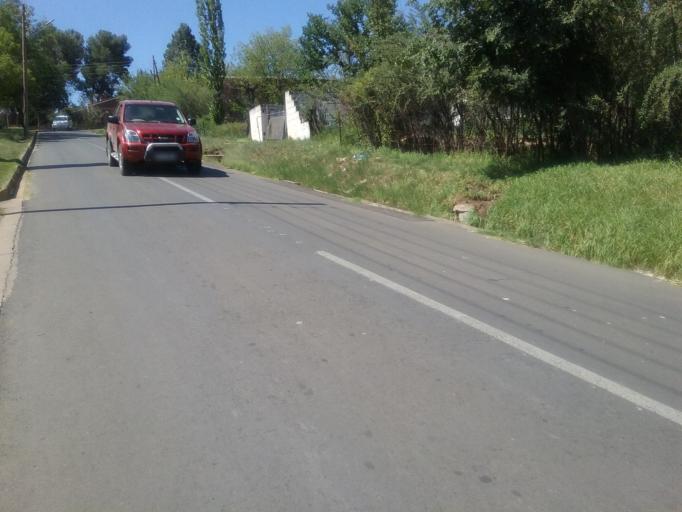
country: LS
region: Maseru
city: Maseru
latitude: -29.3087
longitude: 27.4758
